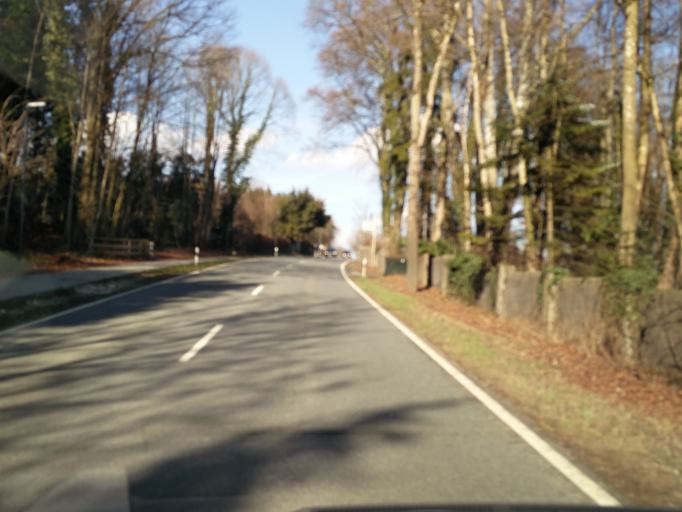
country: DE
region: Bavaria
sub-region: Upper Bavaria
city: Prien am Chiemsee
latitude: 47.8626
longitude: 12.3388
